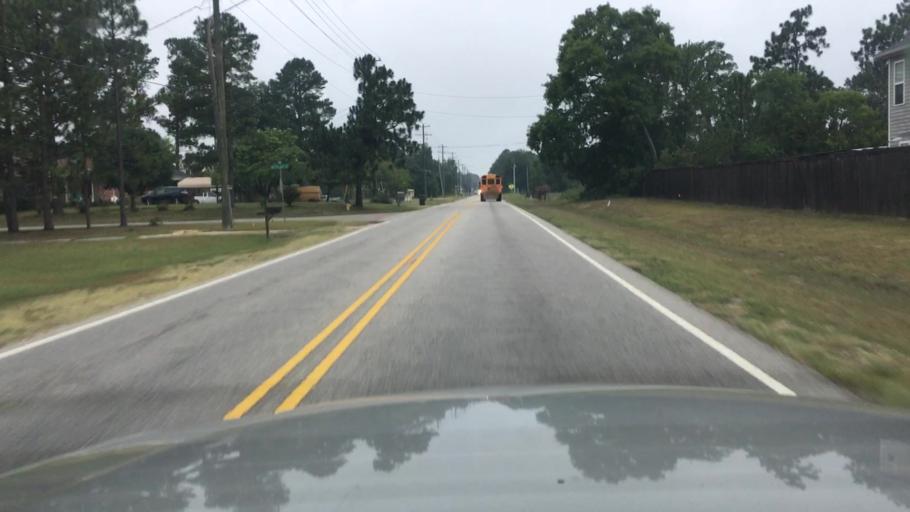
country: US
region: North Carolina
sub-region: Cumberland County
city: Hope Mills
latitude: 34.9761
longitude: -78.9767
